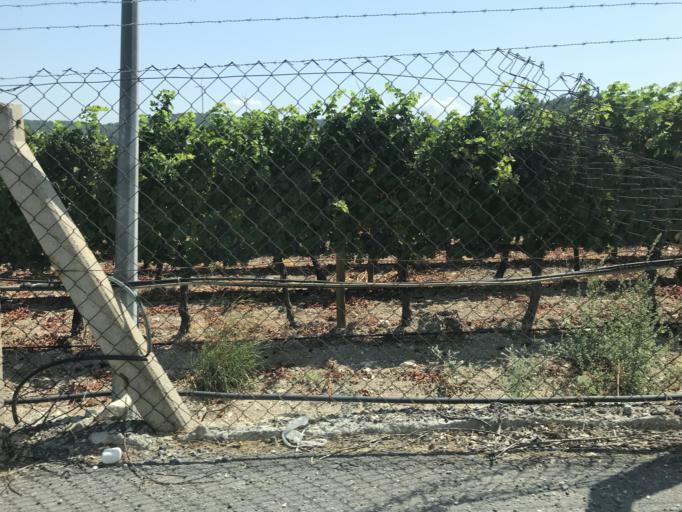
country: TR
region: Izmir
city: Urla
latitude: 38.2533
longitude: 26.7384
